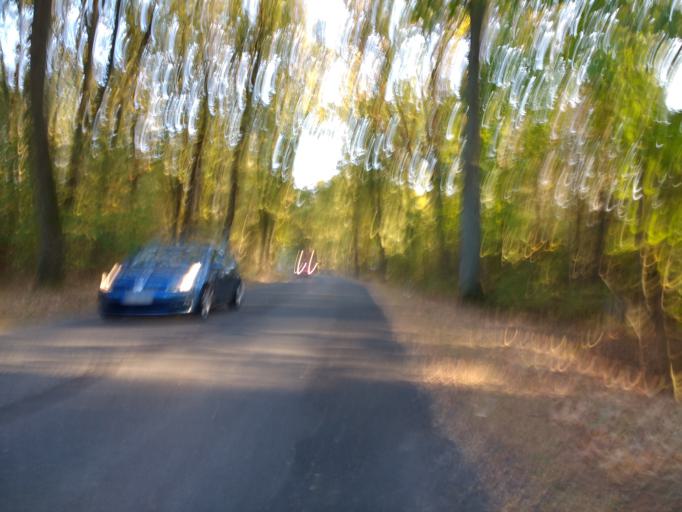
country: DE
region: Lower Saxony
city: Gifhorn
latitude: 52.4647
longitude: 10.5702
